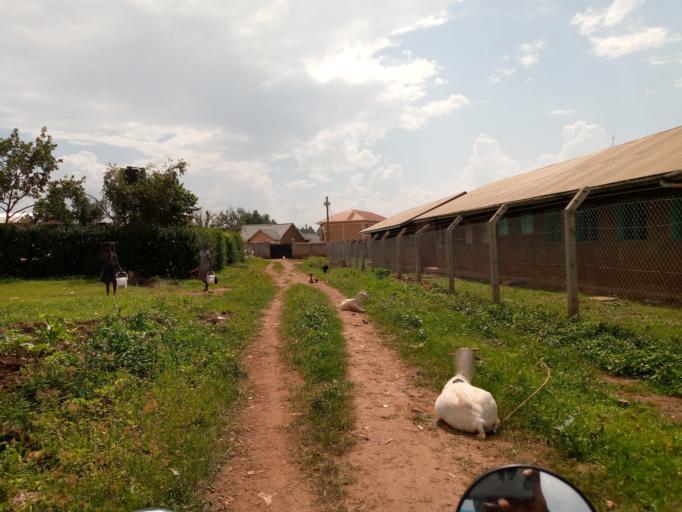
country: UG
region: Eastern Region
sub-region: Mbale District
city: Mbale
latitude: 1.0848
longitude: 34.1593
